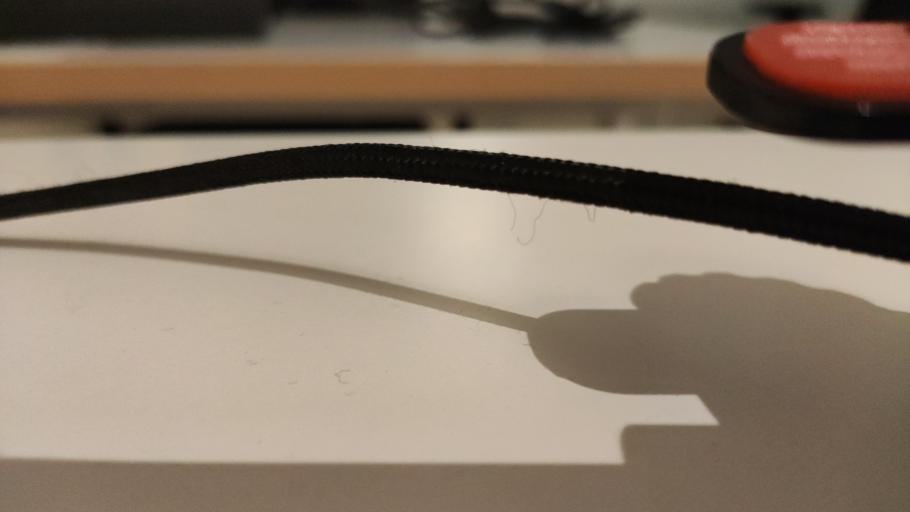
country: RU
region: Moskovskaya
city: Malaya Dubna
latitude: 55.8446
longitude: 38.9651
